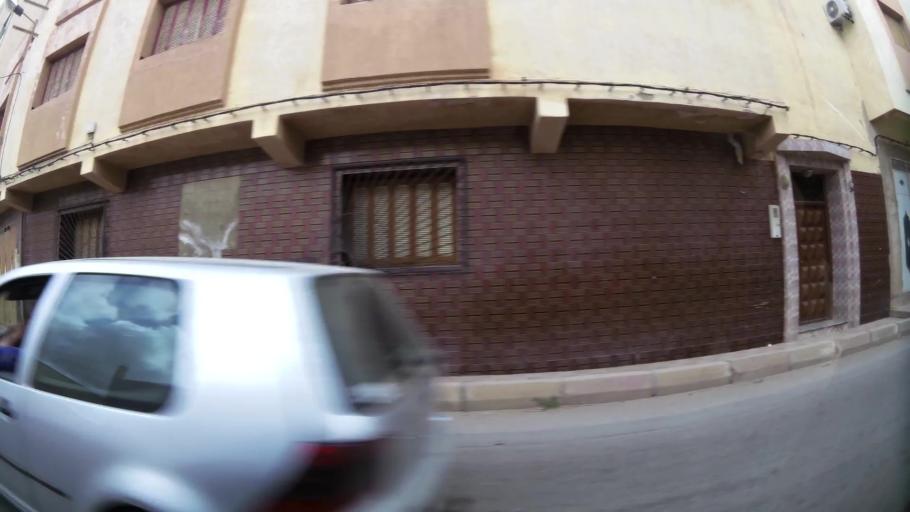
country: MA
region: Oriental
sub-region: Nador
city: Nador
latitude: 35.1627
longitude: -2.9403
